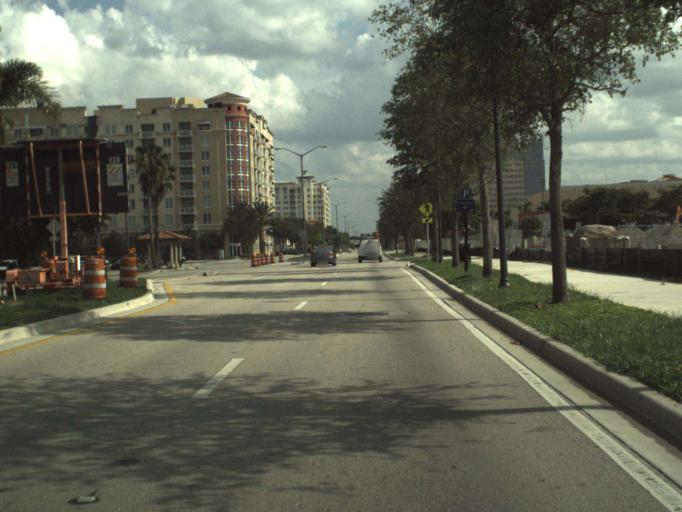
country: US
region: Florida
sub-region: Palm Beach County
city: West Palm Beach
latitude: 26.7130
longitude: -80.0551
